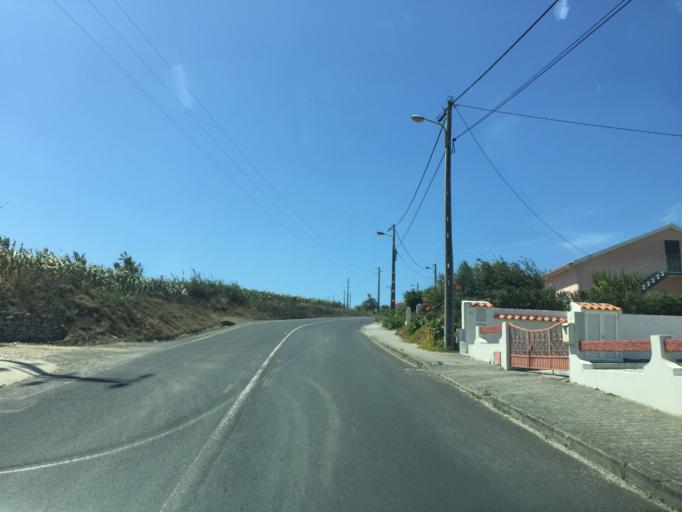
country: PT
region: Lisbon
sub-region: Lourinha
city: Lourinha
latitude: 39.2199
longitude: -9.3195
